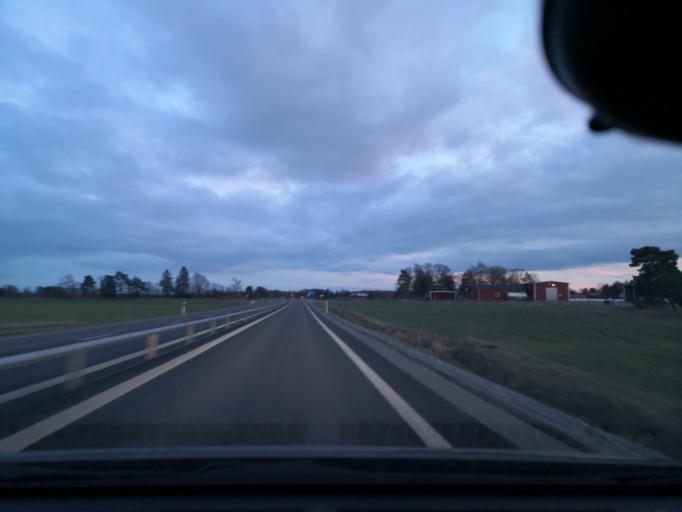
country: SE
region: Uppsala
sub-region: Enkopings Kommun
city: Enkoping
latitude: 59.6880
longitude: 17.0345
